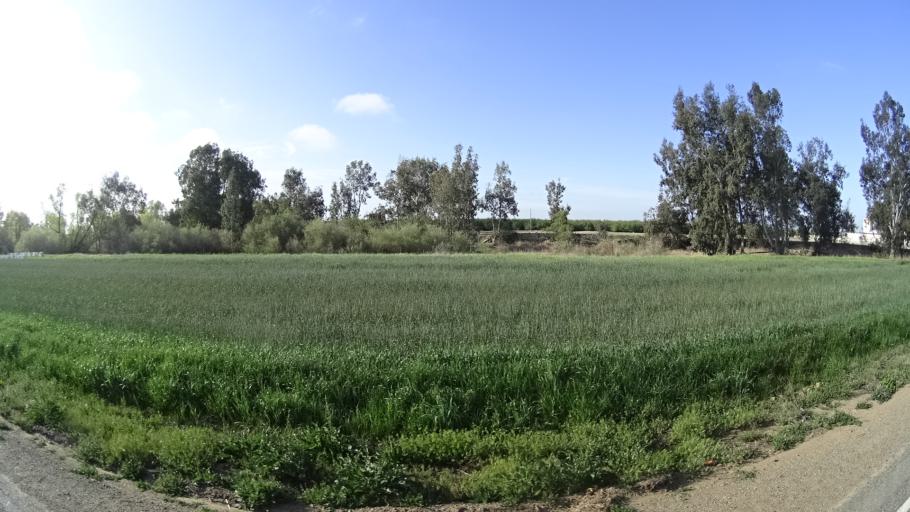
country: US
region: California
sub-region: Glenn County
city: Willows
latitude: 39.5840
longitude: -122.1897
